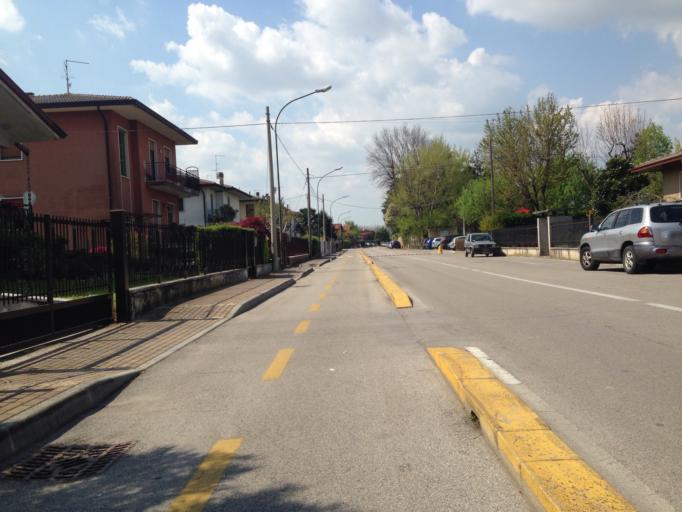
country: IT
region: Veneto
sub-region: Provincia di Verona
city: Zevio
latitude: 45.3702
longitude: 11.1122
